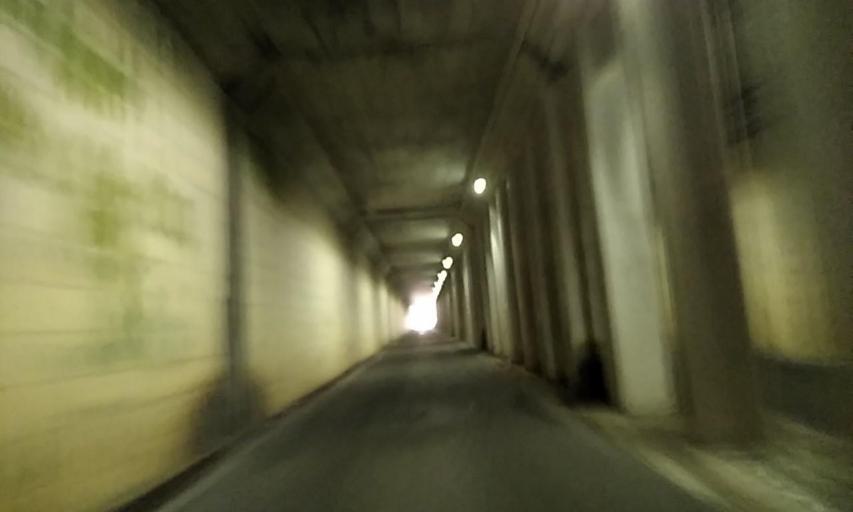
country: JP
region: Wakayama
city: Tanabe
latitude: 33.6658
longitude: 135.3547
